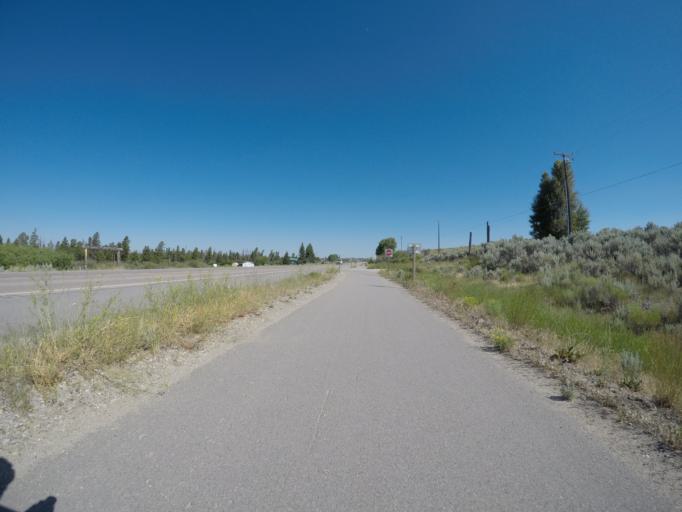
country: US
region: Wyoming
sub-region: Sublette County
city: Pinedale
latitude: 42.8479
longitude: -109.8487
